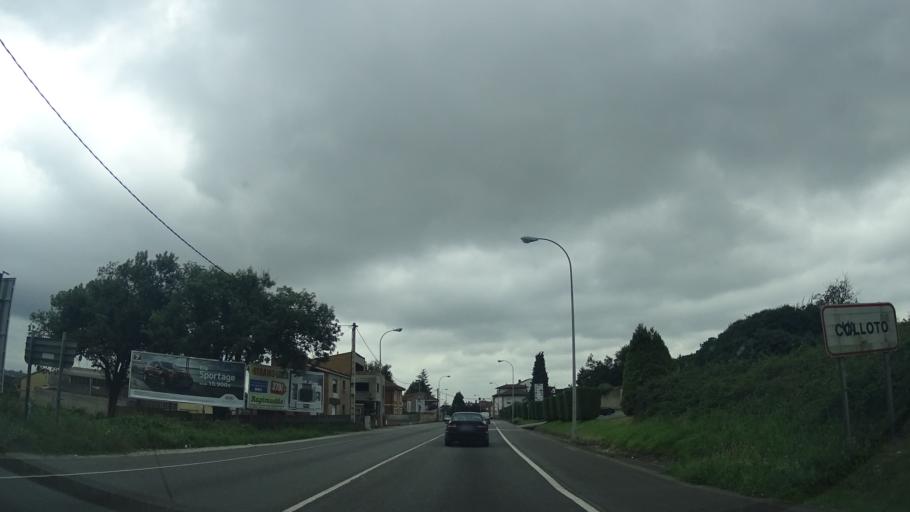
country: ES
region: Asturias
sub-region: Province of Asturias
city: Lugones
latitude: 43.3779
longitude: -5.8012
